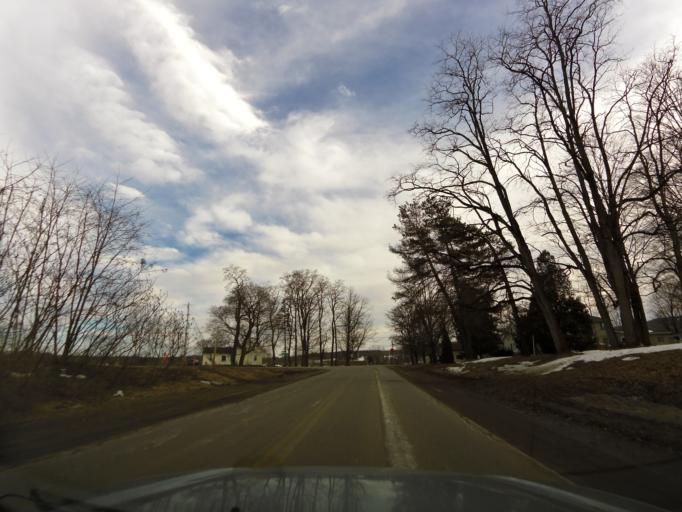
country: US
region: New York
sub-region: Cattaraugus County
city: Yorkshire
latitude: 42.5233
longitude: -78.5085
